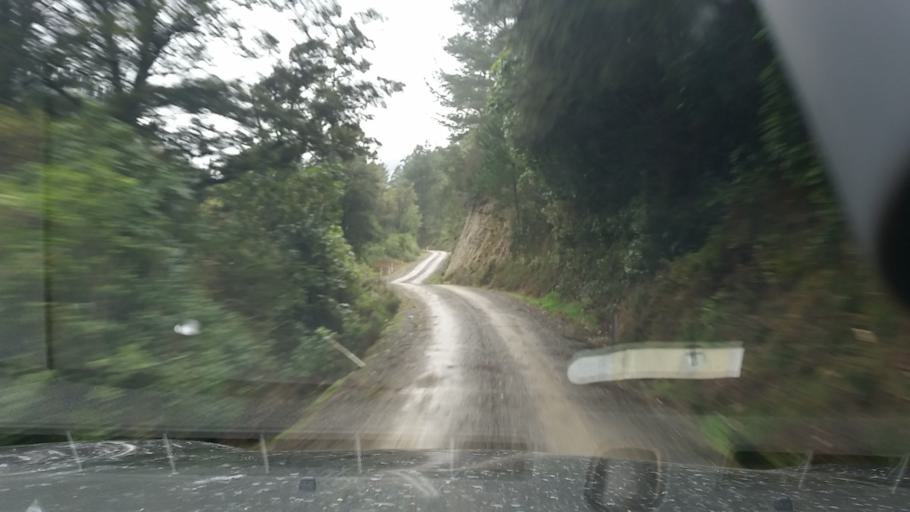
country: NZ
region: Nelson
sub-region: Nelson City
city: Nelson
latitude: -41.3599
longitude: 173.6180
